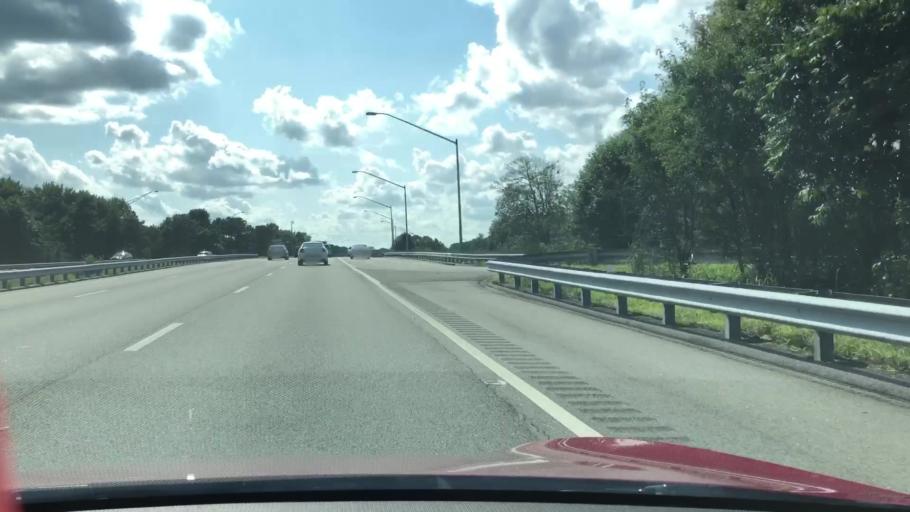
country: US
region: Virginia
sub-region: City of Virginia Beach
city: Virginia Beach
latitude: 36.8471
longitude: -75.9919
